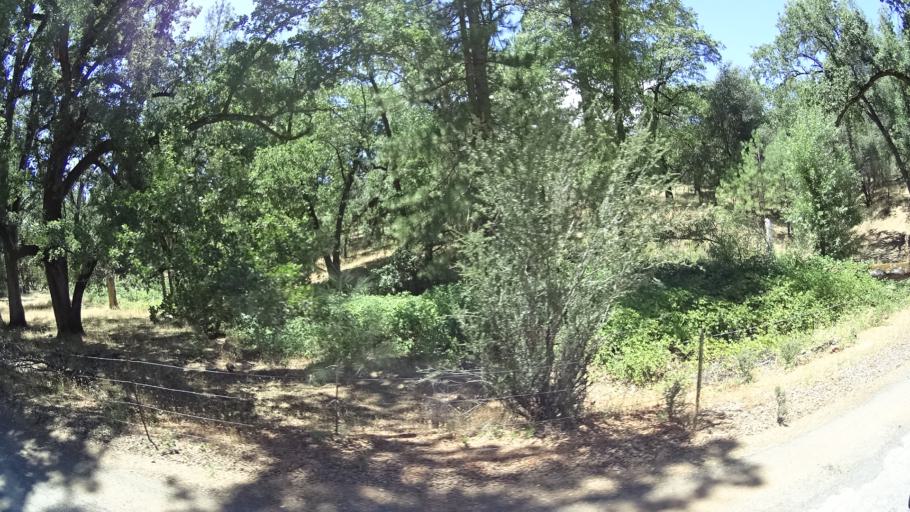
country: US
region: California
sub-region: Calaveras County
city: Forest Meadows
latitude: 38.2315
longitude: -120.4498
